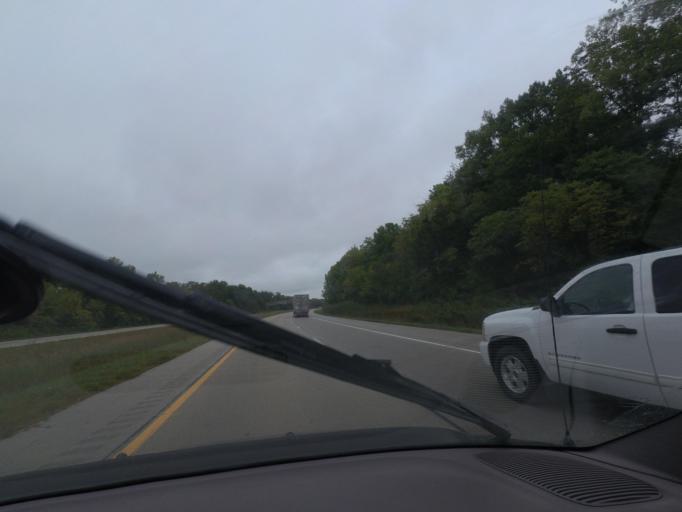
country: US
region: Illinois
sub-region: Sangamon County
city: Riverton
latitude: 39.8230
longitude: -89.5497
